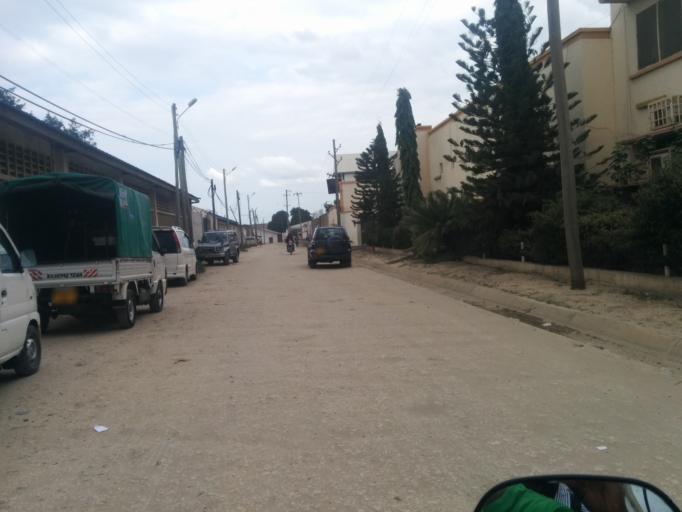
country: TZ
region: Dar es Salaam
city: Dar es Salaam
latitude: -6.8310
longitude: 39.2766
